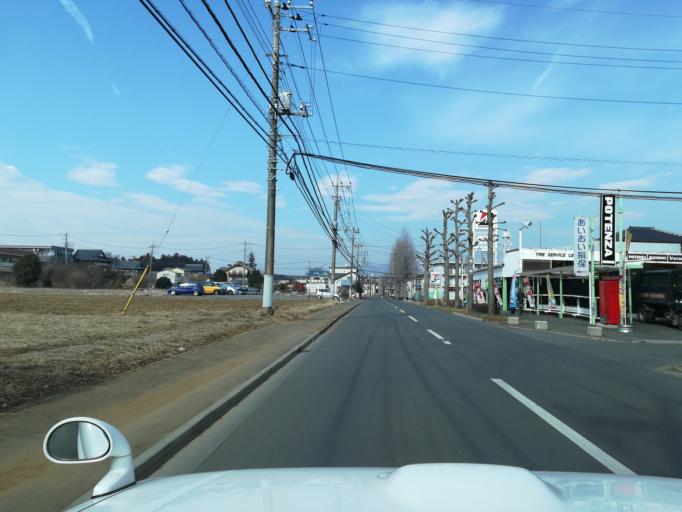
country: JP
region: Ibaraki
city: Naka
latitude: 36.0986
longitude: 140.0985
